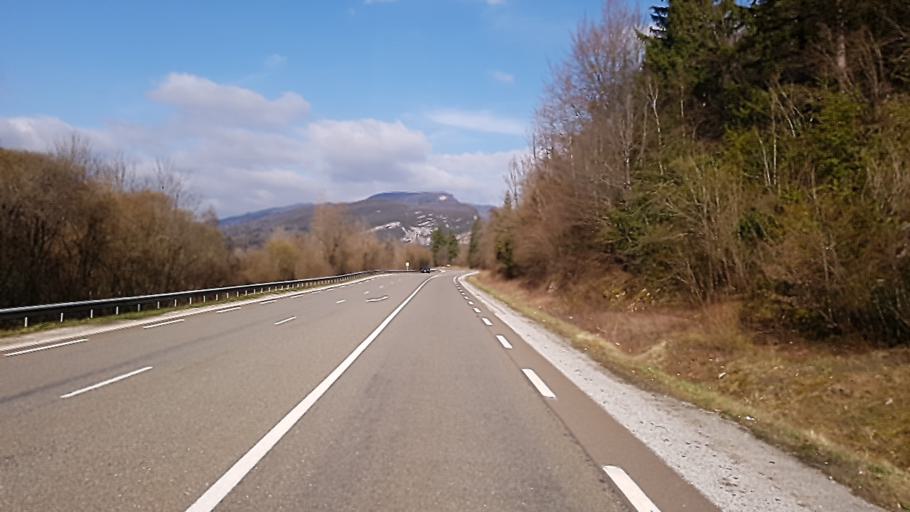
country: FR
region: Rhone-Alpes
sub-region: Departement de l'Ain
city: Dortan
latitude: 46.3550
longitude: 5.6950
